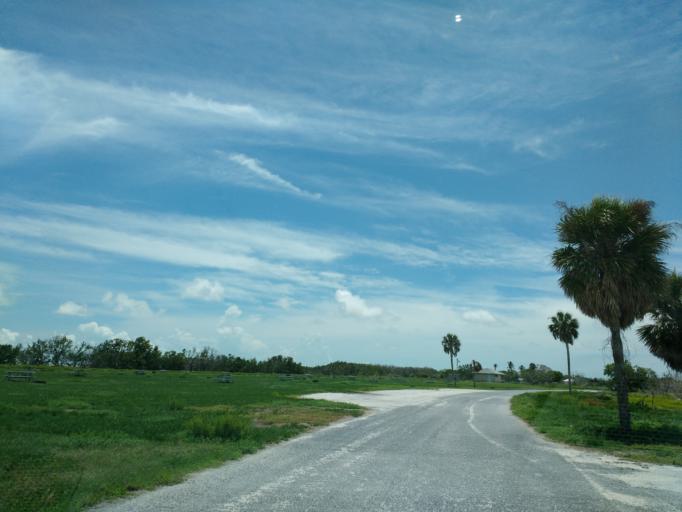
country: US
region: Florida
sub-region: Monroe County
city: Islamorada
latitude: 25.1374
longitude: -80.9352
